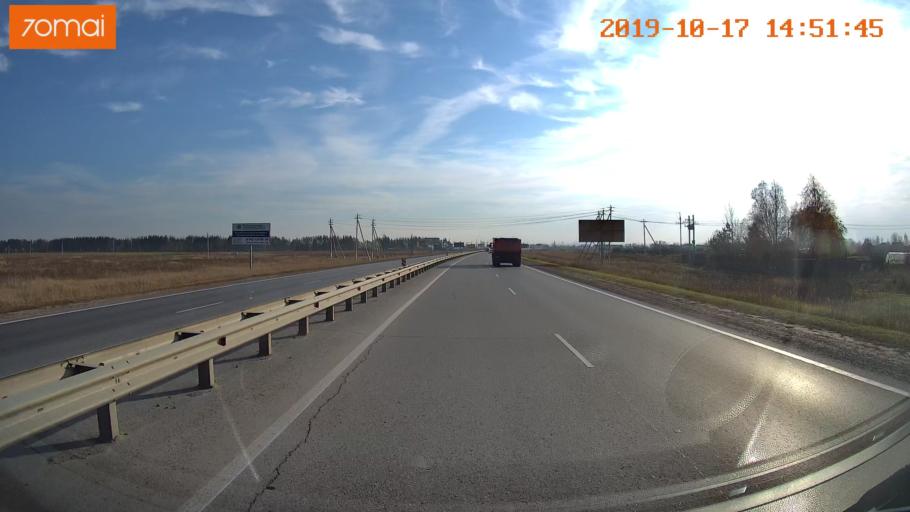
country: RU
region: Rjazan
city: Polyany
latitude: 54.7145
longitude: 39.8481
